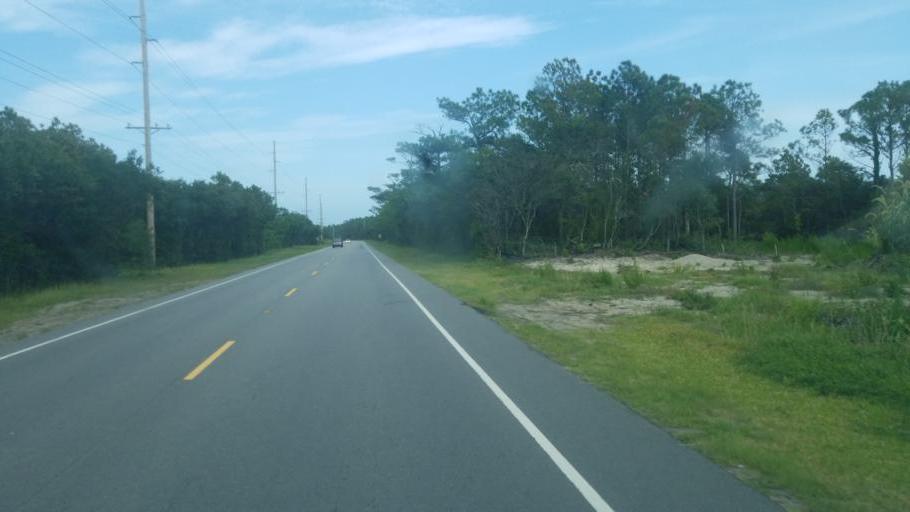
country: US
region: North Carolina
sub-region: Dare County
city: Buxton
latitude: 35.2530
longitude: -75.5971
